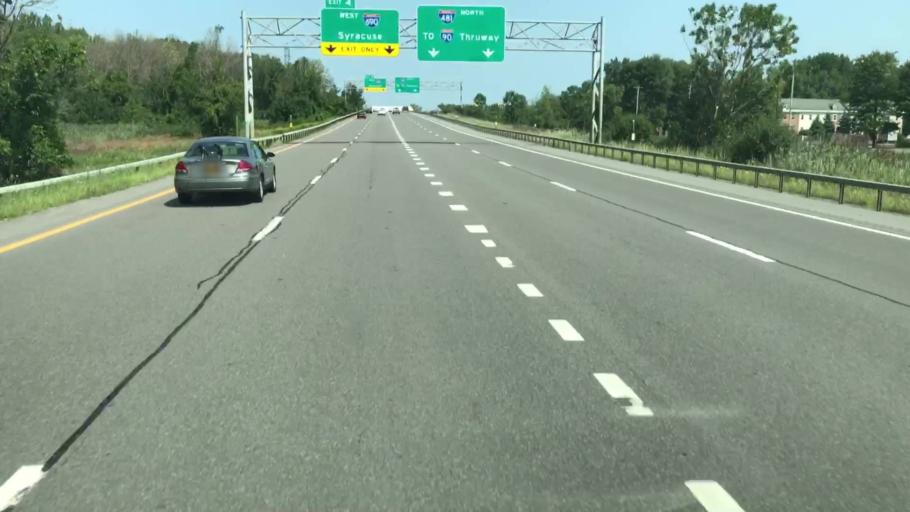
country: US
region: New York
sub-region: Onondaga County
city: East Syracuse
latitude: 43.0470
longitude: -76.0506
